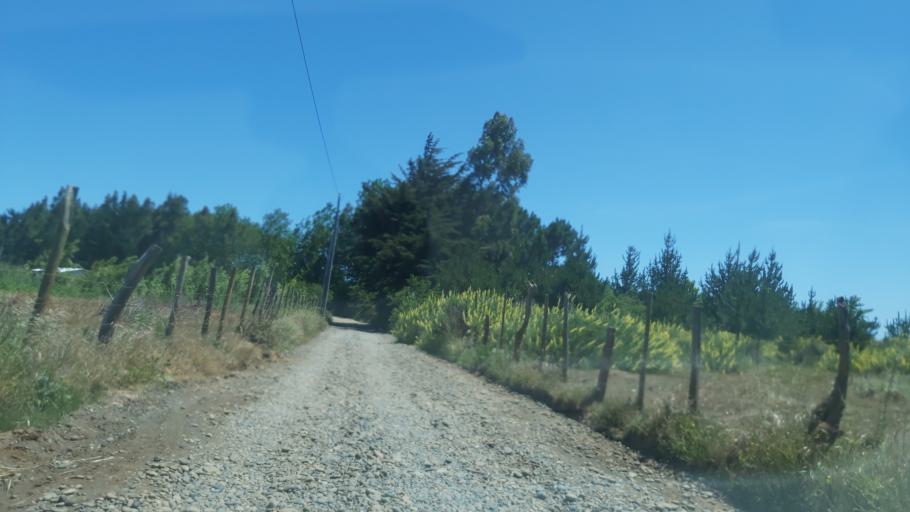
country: CL
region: Maule
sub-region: Provincia de Talca
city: Constitucion
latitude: -35.1627
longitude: -72.2657
